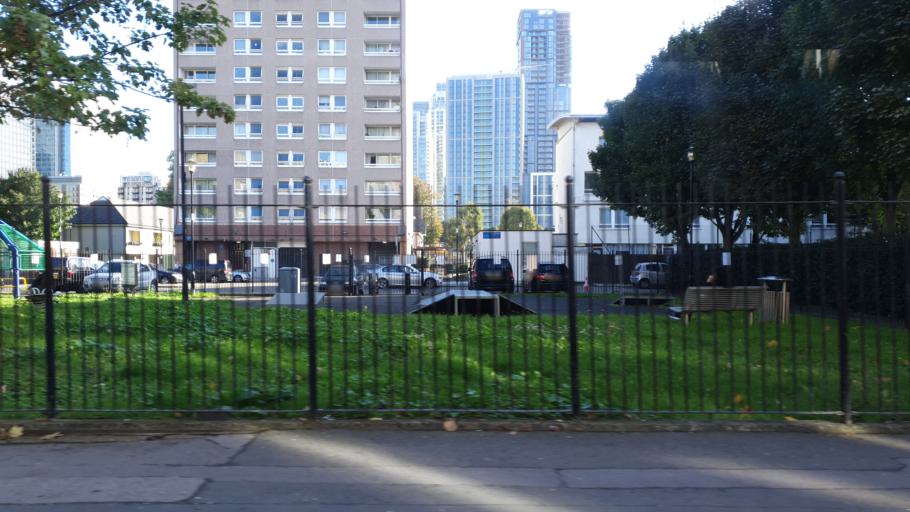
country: GB
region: England
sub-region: Greater London
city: Poplar
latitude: 51.4994
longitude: -0.0257
